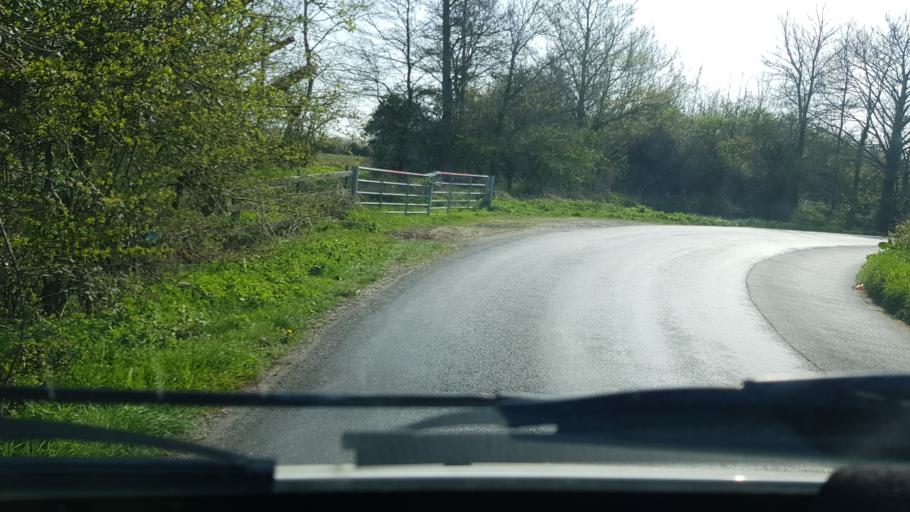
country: GB
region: England
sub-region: West Sussex
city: Chichester
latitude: 50.8265
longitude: -0.8018
